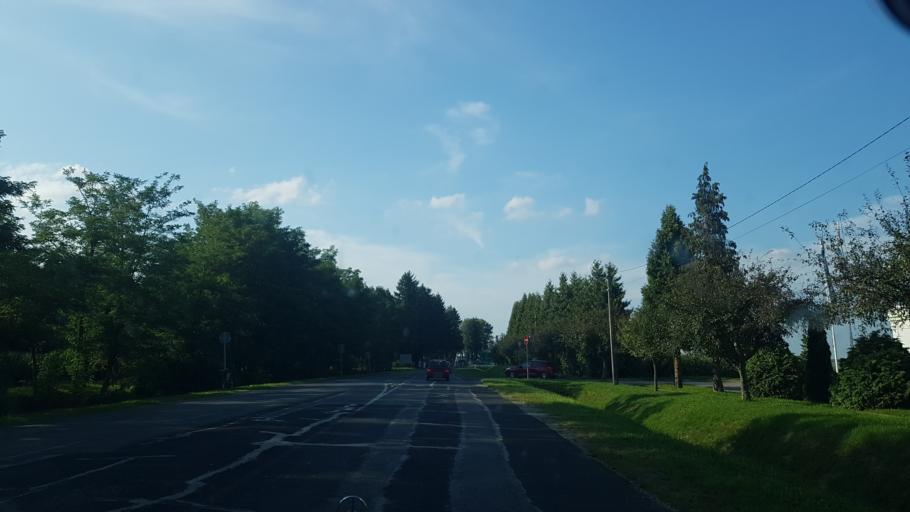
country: HU
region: Somogy
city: Nagyatad
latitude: 46.2407
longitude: 17.3557
